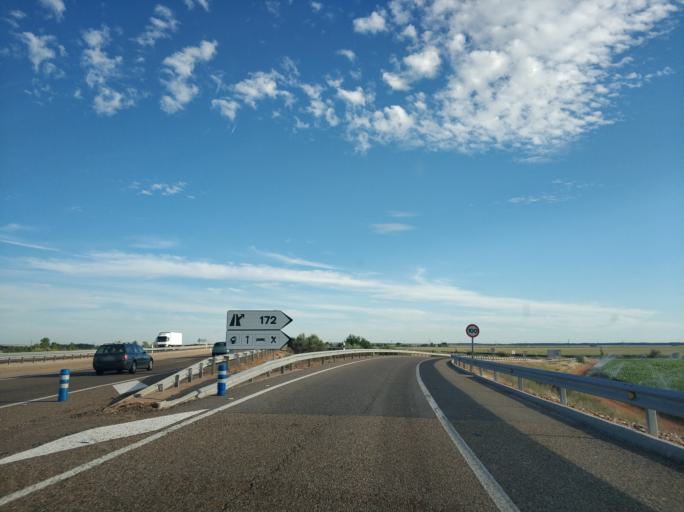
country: ES
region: Castille and Leon
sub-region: Provincia de Leon
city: Villamanan
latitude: 42.3294
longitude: -5.6098
